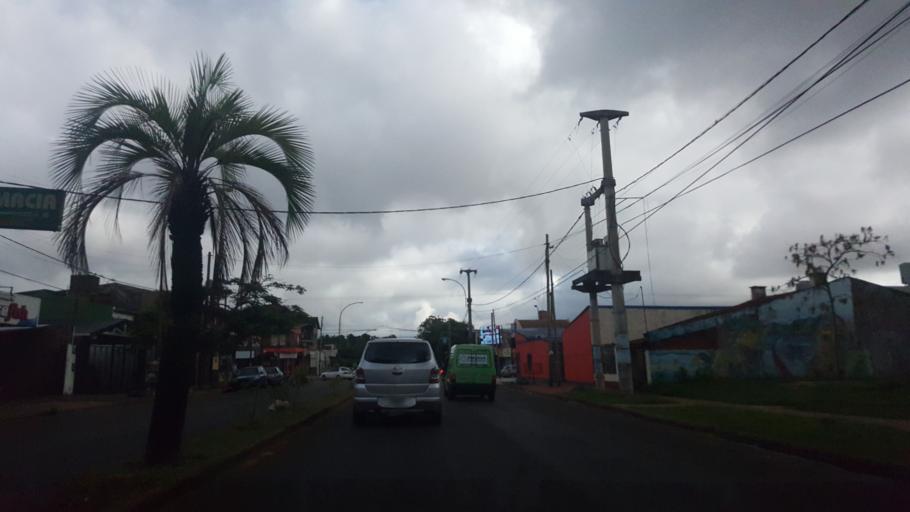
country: AR
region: Misiones
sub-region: Departamento de Capital
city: Posadas
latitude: -27.3699
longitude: -55.9169
